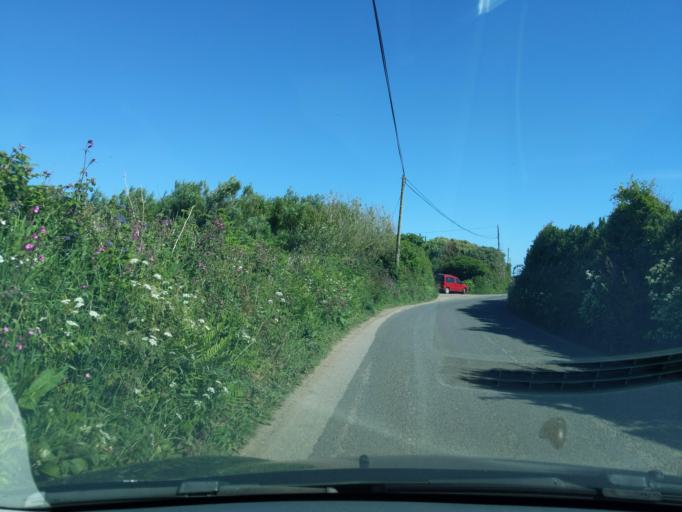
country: GB
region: England
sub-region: Cornwall
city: St. Buryan
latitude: 50.0708
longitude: -5.6119
